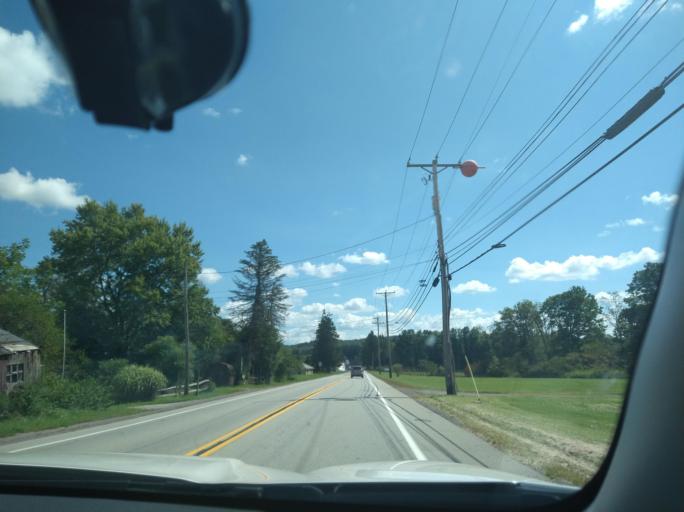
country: US
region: Pennsylvania
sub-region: Somerset County
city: Milford
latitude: 40.0381
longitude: -79.2162
